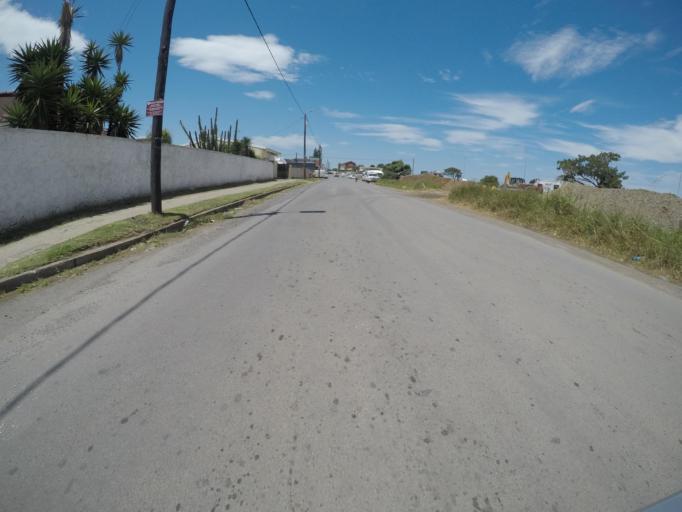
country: ZA
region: Eastern Cape
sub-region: Buffalo City Metropolitan Municipality
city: East London
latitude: -33.0354
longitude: 27.8531
